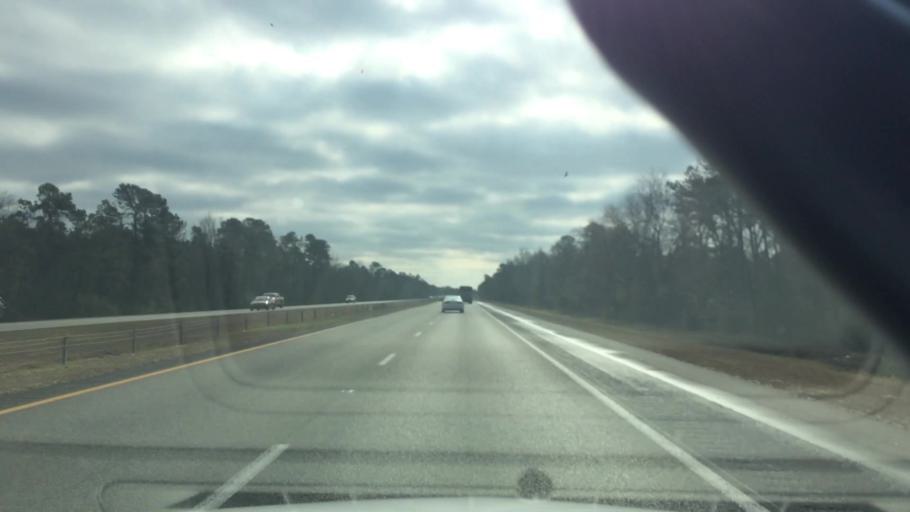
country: US
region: North Carolina
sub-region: Pender County
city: Rocky Point
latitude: 34.4047
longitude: -77.8720
